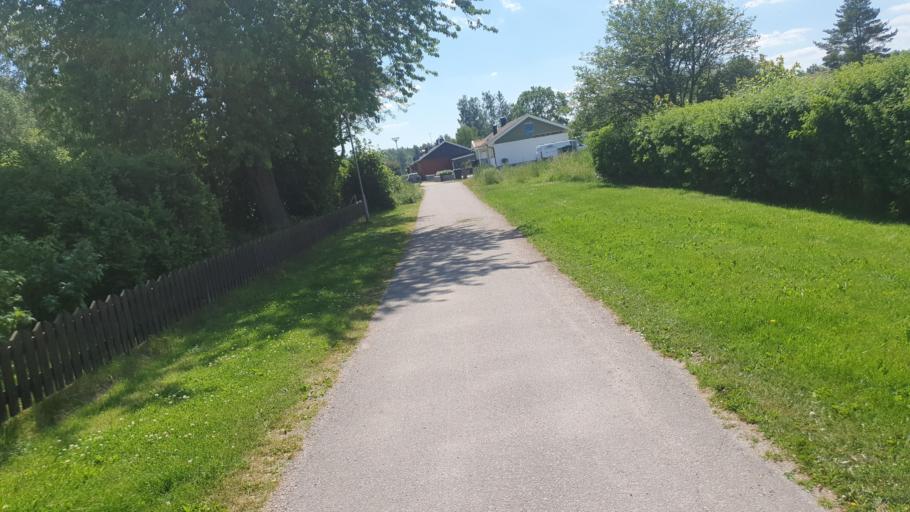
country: SE
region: Uppsala
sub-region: Osthammars Kommun
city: Gimo
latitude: 60.1709
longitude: 18.1772
